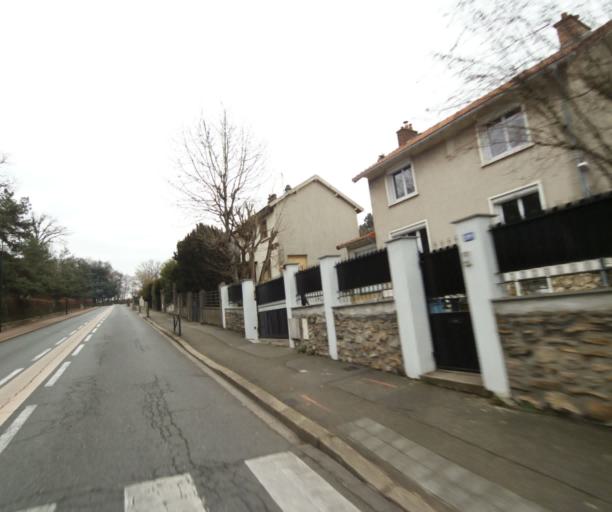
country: FR
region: Ile-de-France
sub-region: Departement des Hauts-de-Seine
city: Vaucresson
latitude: 48.8406
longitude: 2.1650
